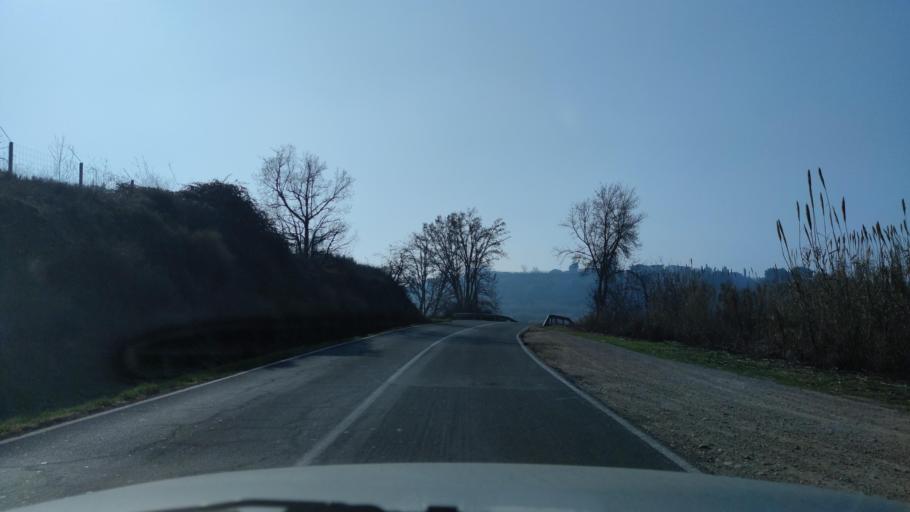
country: ES
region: Catalonia
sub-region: Provincia de Lleida
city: Sunyer
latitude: 41.5604
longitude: 0.5752
